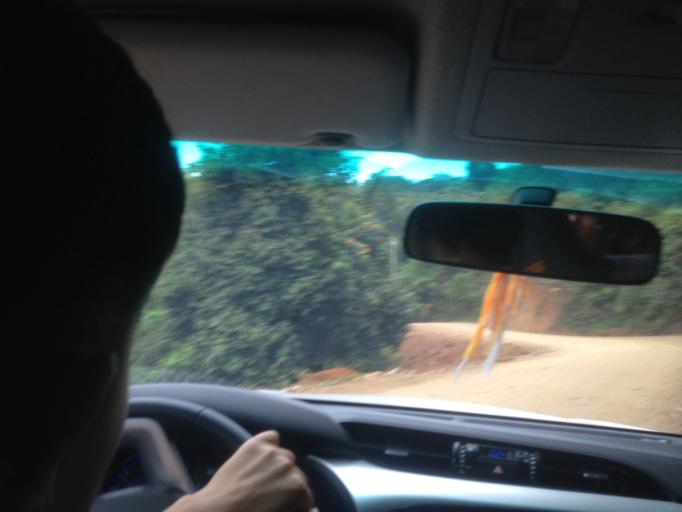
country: TH
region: Nan
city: Chaloem Phra Kiat
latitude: 19.9860
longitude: 101.1439
